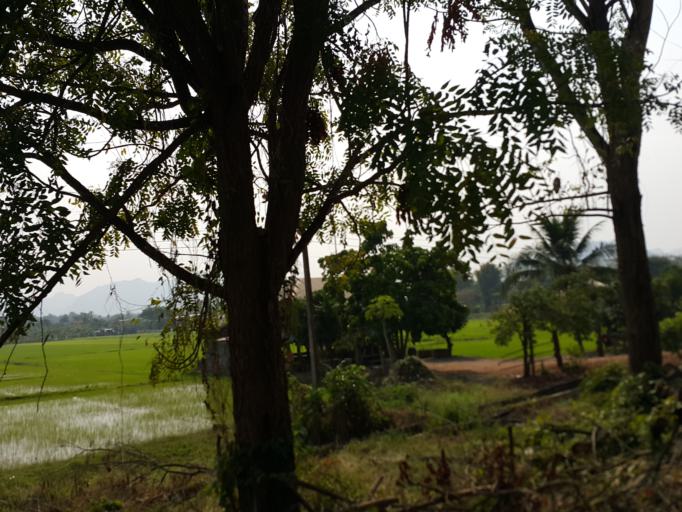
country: TH
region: Sukhothai
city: Thung Saliam
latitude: 17.3316
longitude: 99.5306
